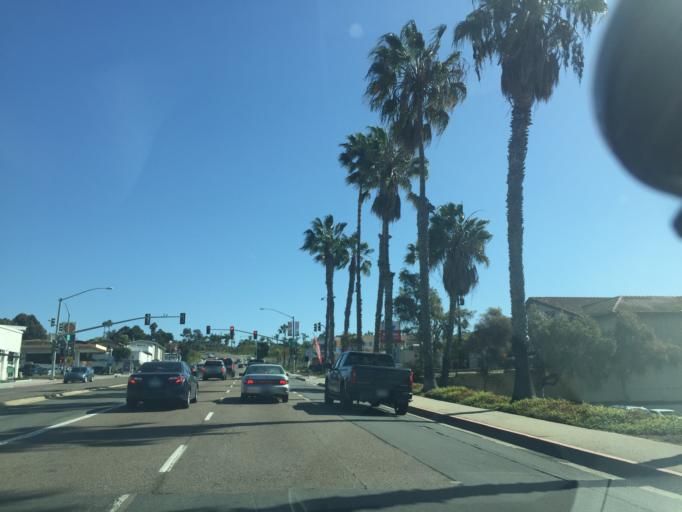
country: US
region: California
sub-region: San Diego County
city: San Diego
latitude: 32.7905
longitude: -117.2042
